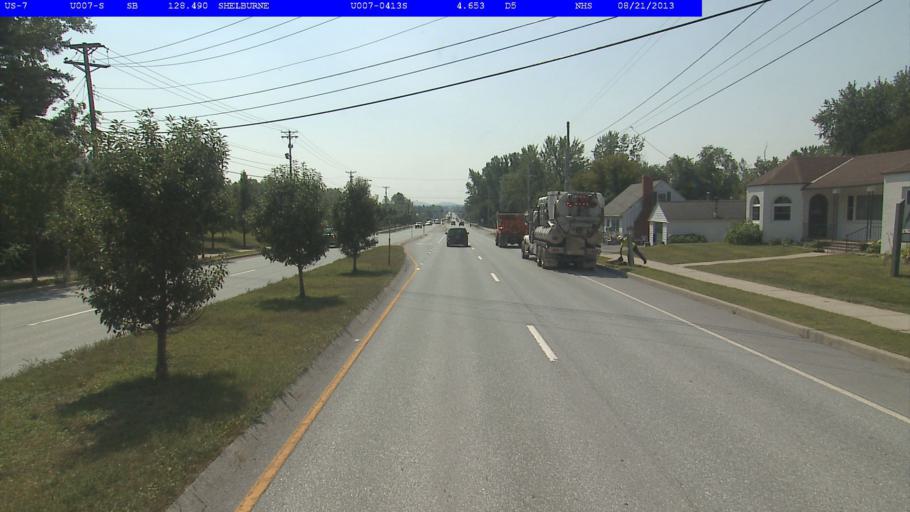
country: US
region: Vermont
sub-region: Chittenden County
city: Burlington
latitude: 44.4146
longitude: -73.2140
